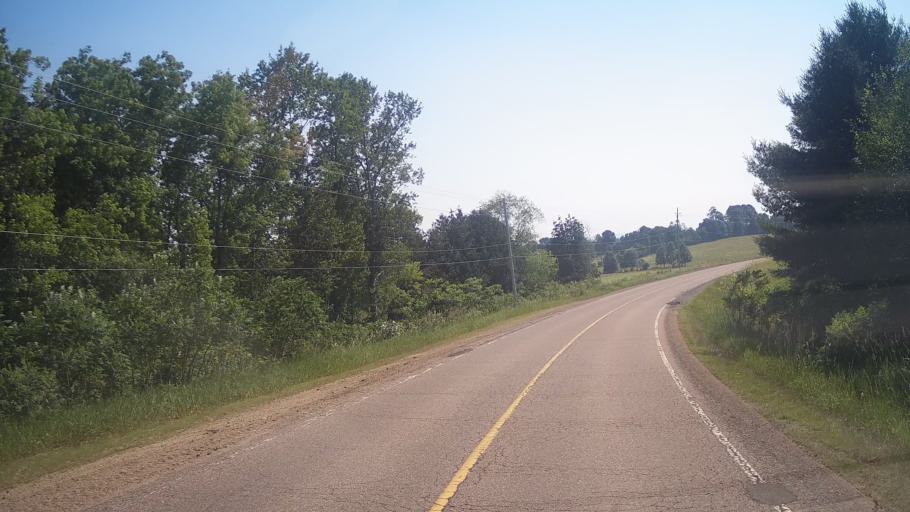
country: CA
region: Ontario
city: Pembroke
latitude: 45.5862
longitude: -77.2271
